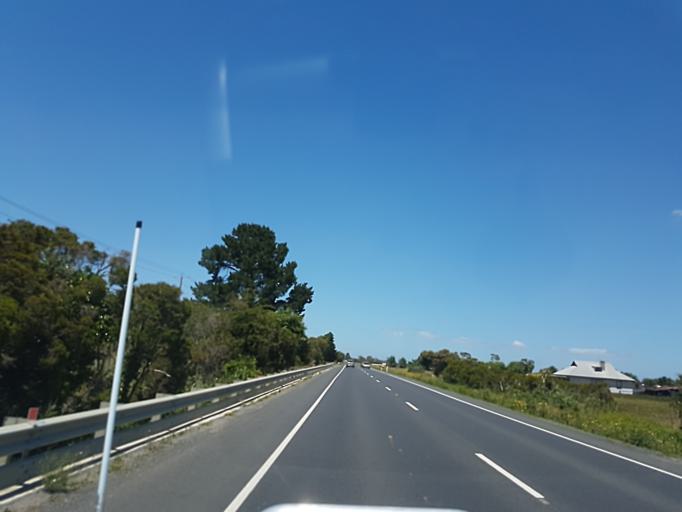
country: AU
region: Victoria
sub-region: Cardinia
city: Pakenham South
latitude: -38.1318
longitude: 145.4895
